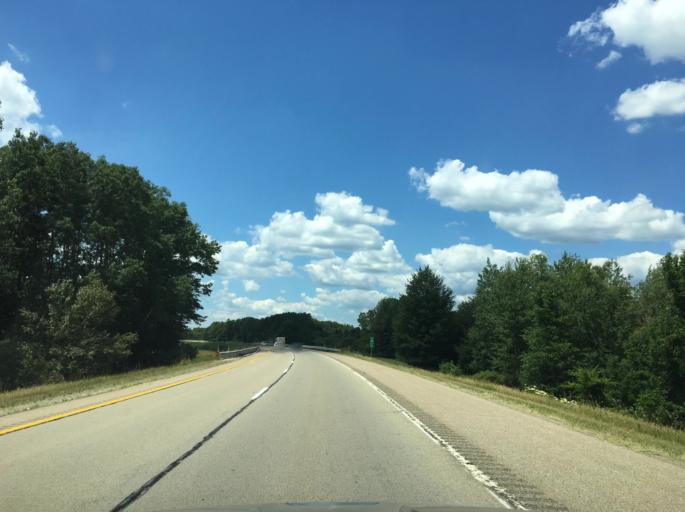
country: US
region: Michigan
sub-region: Clare County
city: Clare
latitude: 43.8840
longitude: -84.8020
